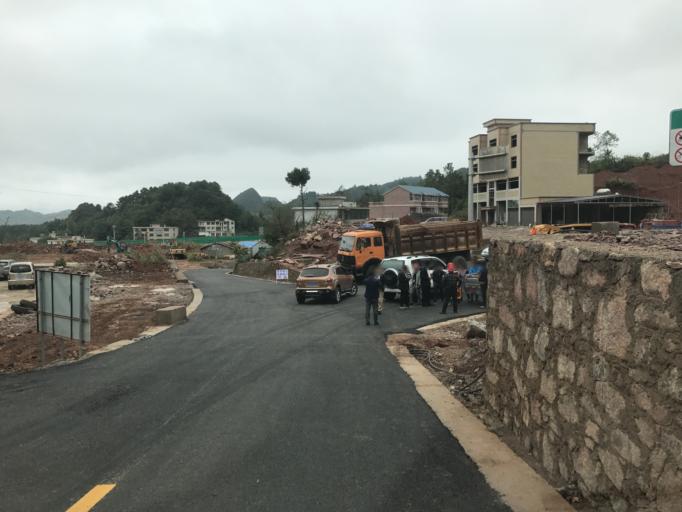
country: CN
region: Guizhou Sheng
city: Supu
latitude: 26.7375
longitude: 106.4370
